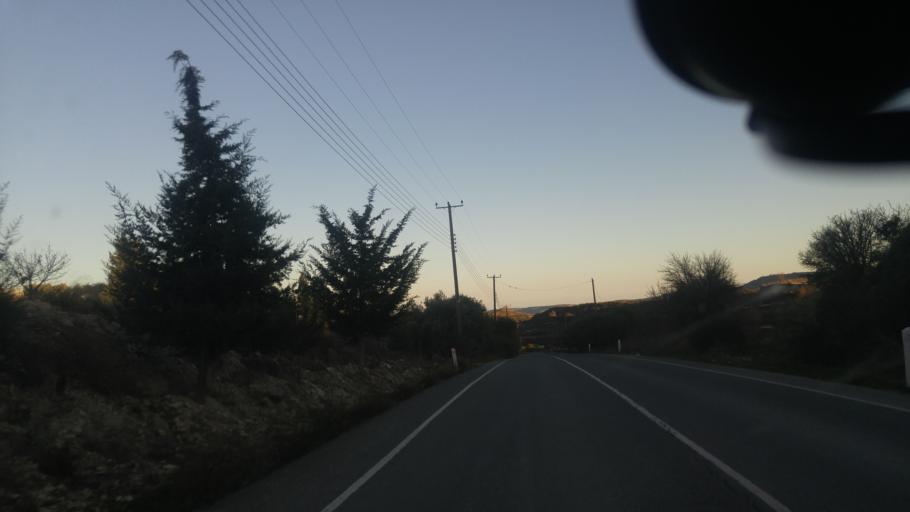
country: CY
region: Limassol
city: Pachna
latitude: 34.7972
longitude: 32.8023
